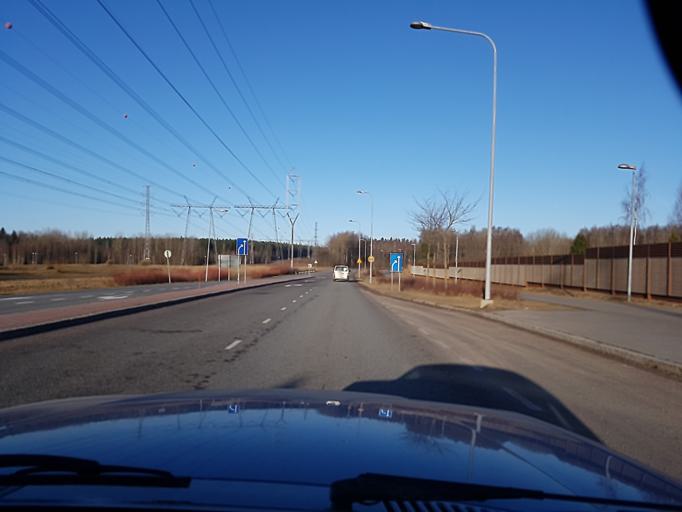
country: FI
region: Uusimaa
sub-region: Helsinki
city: Vantaa
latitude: 60.2899
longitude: 24.9442
